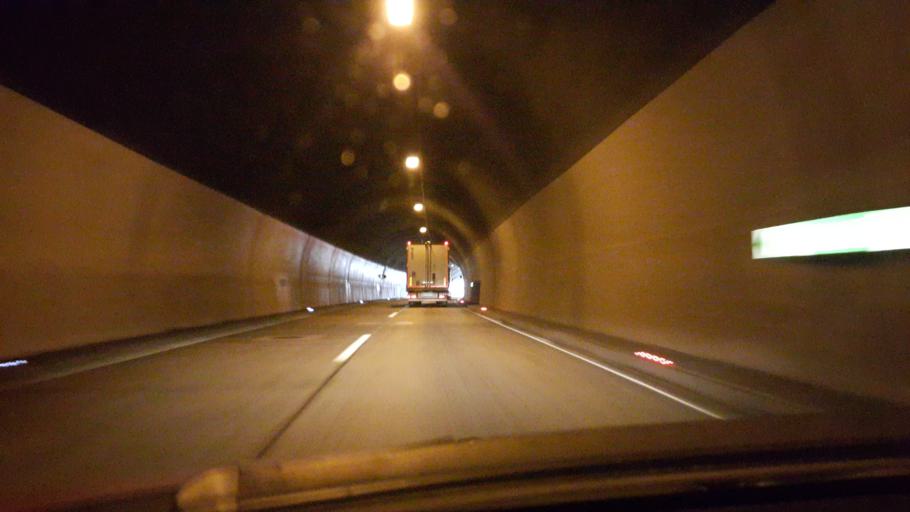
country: SI
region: Slovenska Konjice
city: Slovenske Konjice
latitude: 46.2942
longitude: 15.4398
